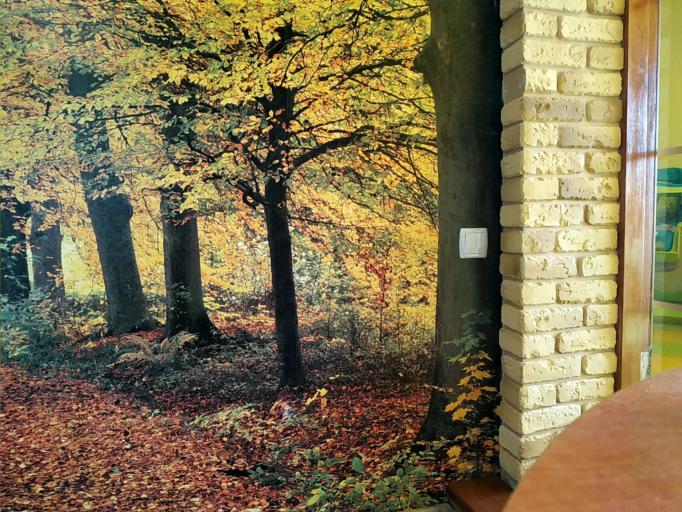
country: RU
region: Novgorod
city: Staraya Russa
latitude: 57.8347
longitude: 31.4763
